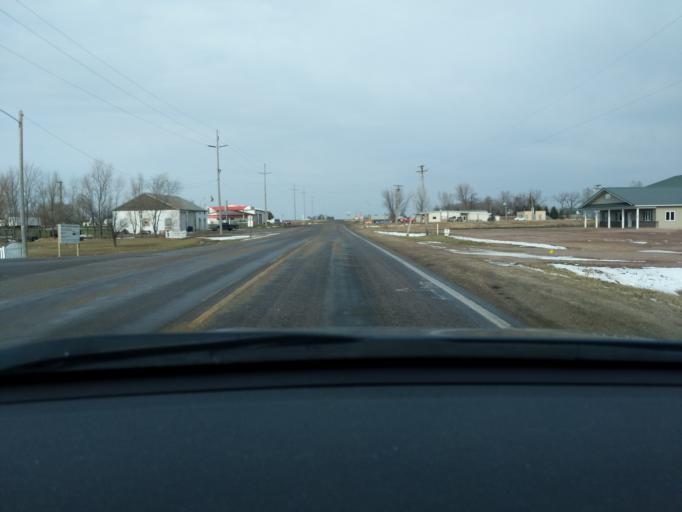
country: US
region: Minnesota
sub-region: Renville County
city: Renville
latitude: 44.7857
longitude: -95.3409
